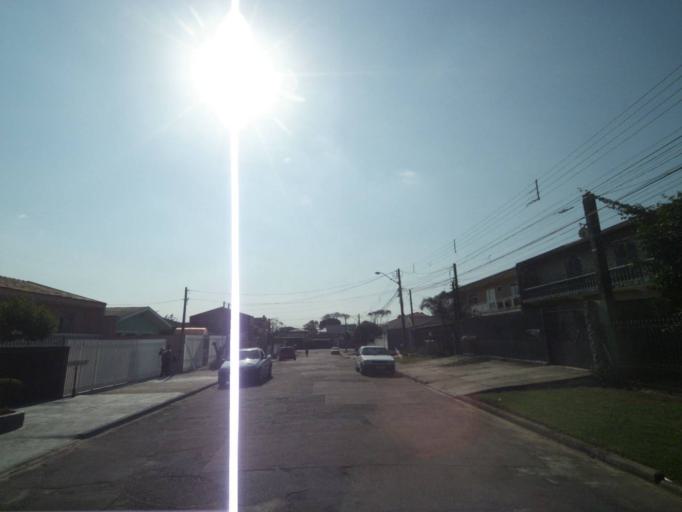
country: BR
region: Parana
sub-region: Curitiba
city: Curitiba
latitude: -25.4873
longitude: -49.3279
